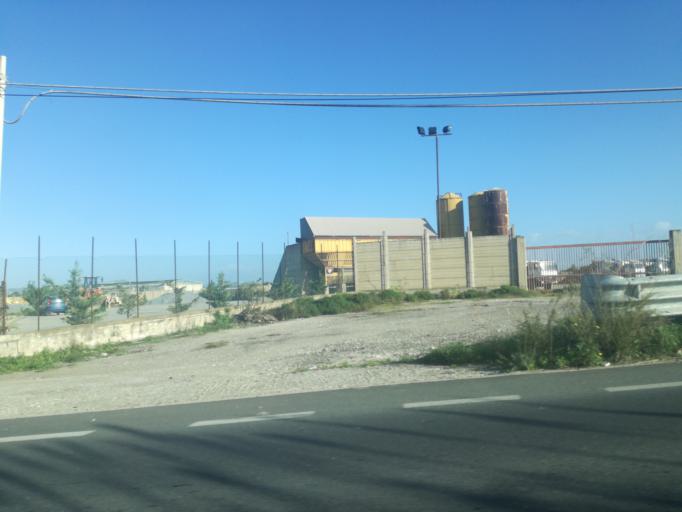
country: IT
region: Sicily
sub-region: Provincia di Caltanissetta
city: Gela
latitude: 37.0611
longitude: 14.2757
